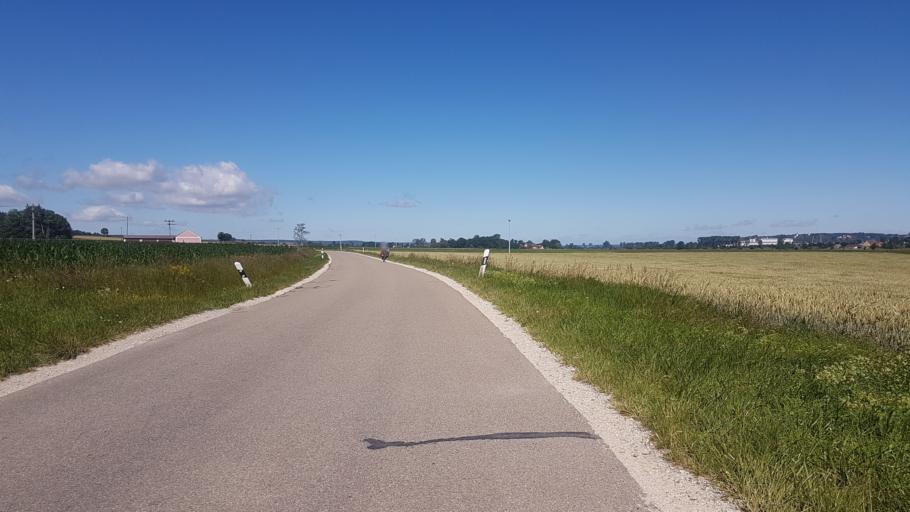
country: DE
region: Bavaria
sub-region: Regierungsbezirk Mittelfranken
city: Herrieden
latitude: 49.2103
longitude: 10.5348
